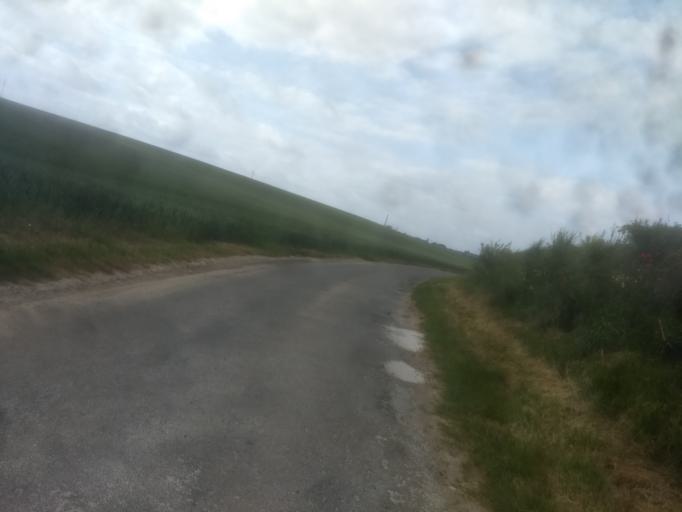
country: FR
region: Nord-Pas-de-Calais
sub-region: Departement du Pas-de-Calais
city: Feuchy
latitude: 50.2868
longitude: 2.8371
